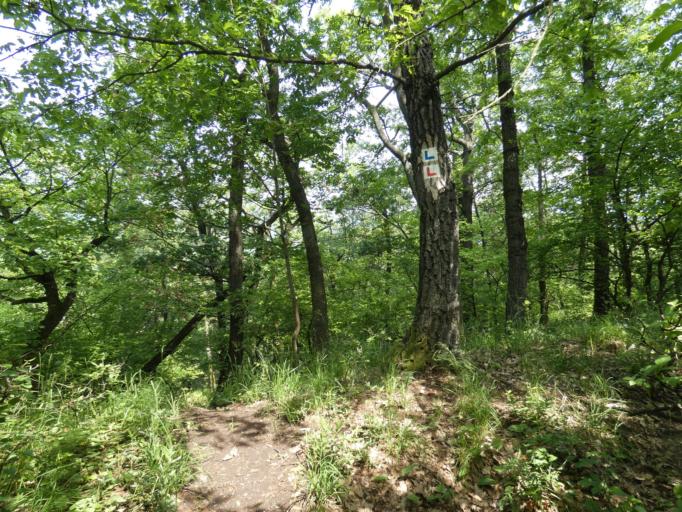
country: HU
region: Pest
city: Szob
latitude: 47.8604
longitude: 18.8483
